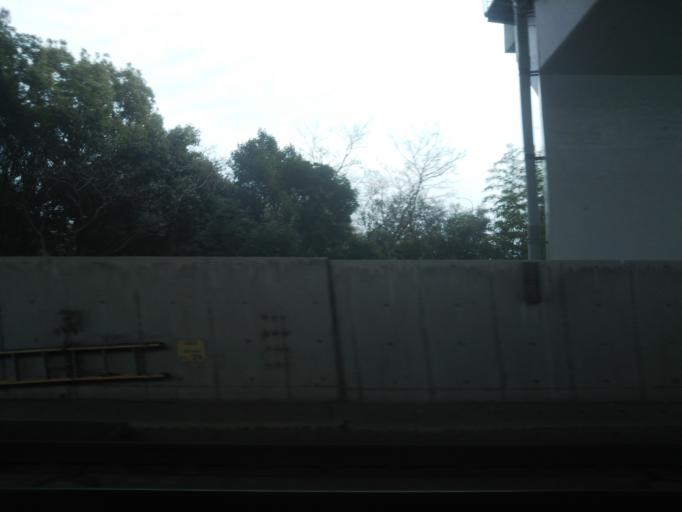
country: JP
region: Kagawa
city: Sakaidecho
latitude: 34.4220
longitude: 133.8038
